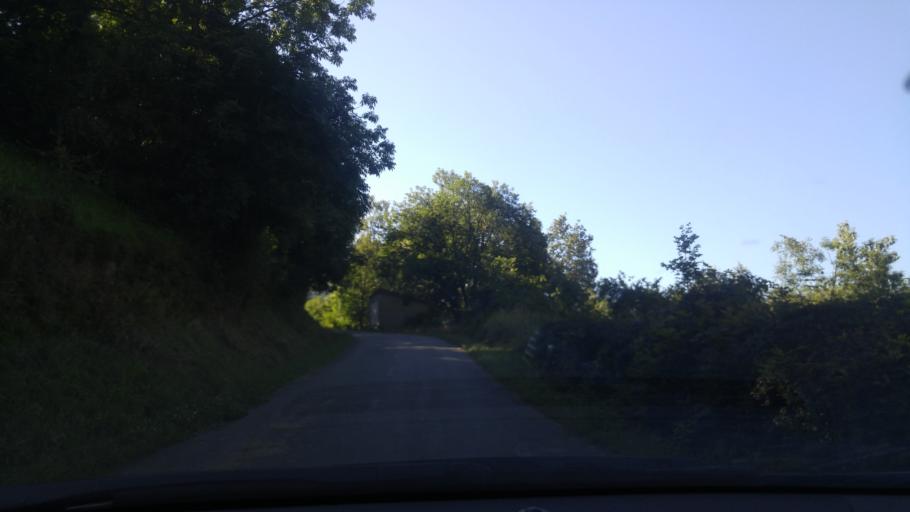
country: ES
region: Asturias
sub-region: Province of Asturias
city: Barzana
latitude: 43.1748
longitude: -5.9715
